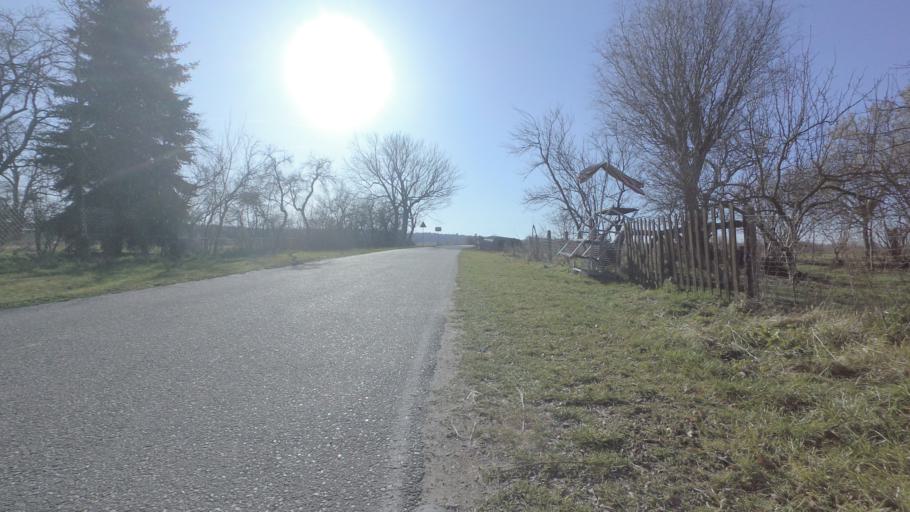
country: DE
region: Brandenburg
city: Luckenwalde
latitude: 52.0396
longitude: 13.1360
